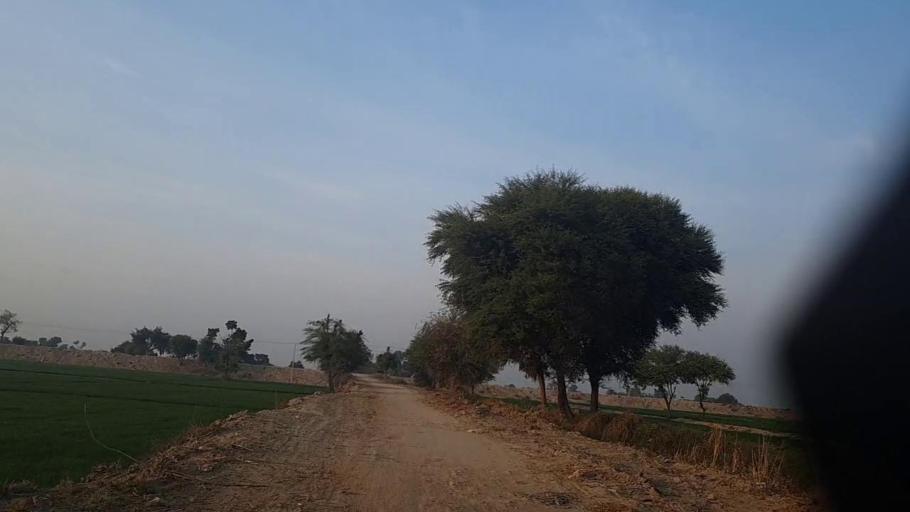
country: PK
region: Sindh
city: Sakrand
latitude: 26.1373
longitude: 68.2256
